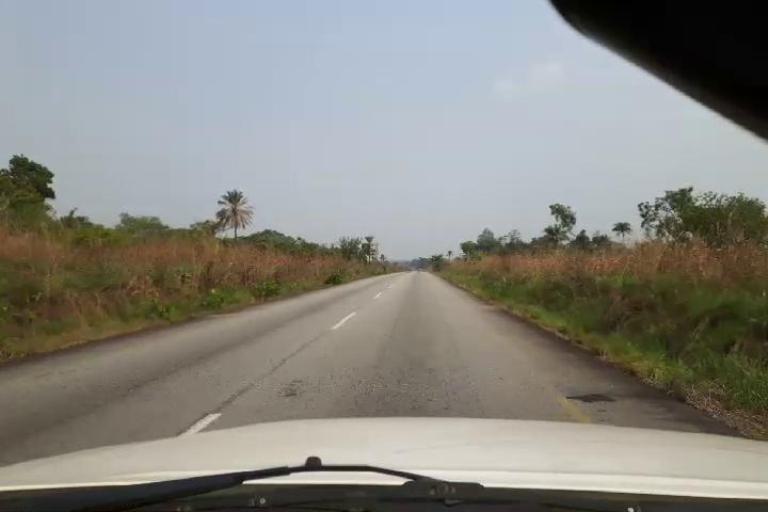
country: SL
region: Southern Province
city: Baiima
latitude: 8.1511
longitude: -11.9110
